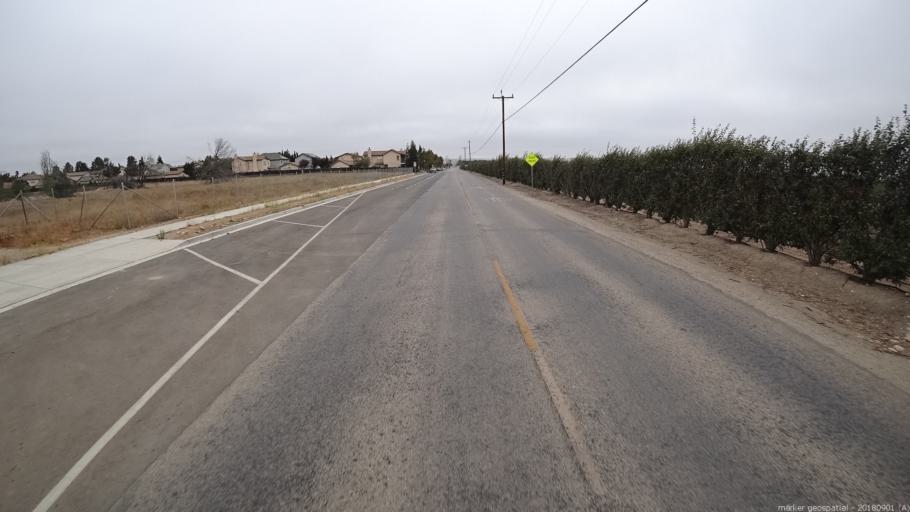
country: US
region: California
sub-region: Monterey County
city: Greenfield
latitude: 36.3111
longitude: -121.2530
